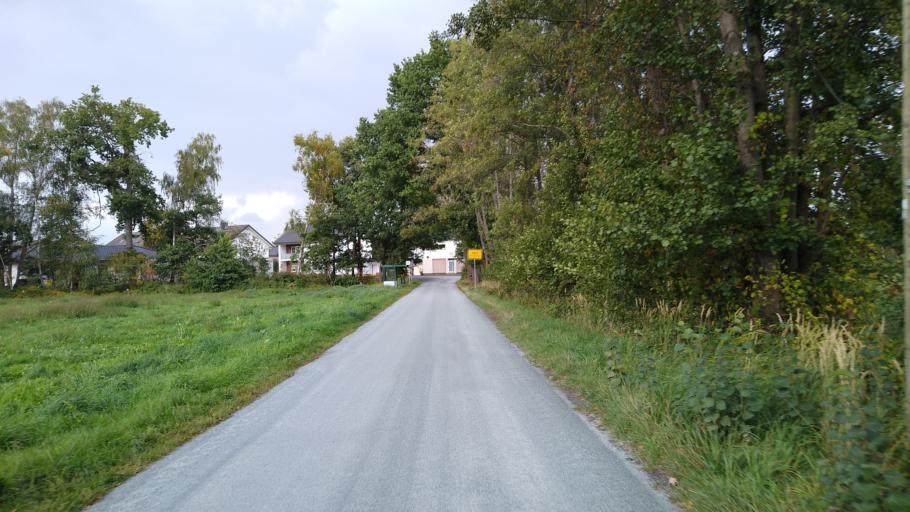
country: DE
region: North Rhine-Westphalia
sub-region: Regierungsbezirk Detmold
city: Verl
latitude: 51.8692
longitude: 8.4770
